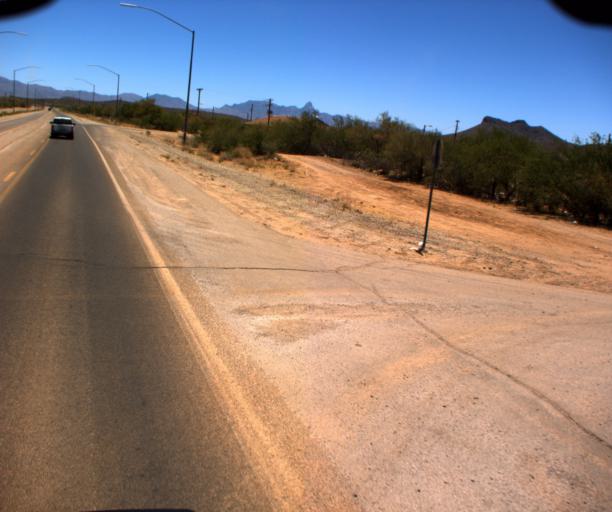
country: US
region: Arizona
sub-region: Pima County
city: Sells
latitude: 31.9175
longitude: -111.8753
